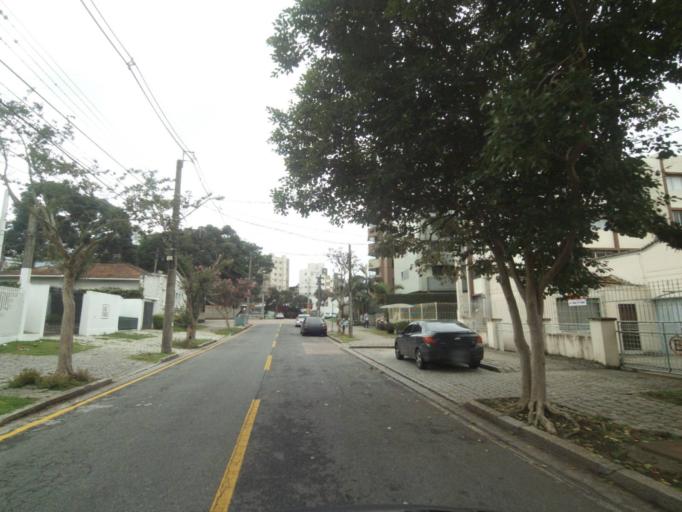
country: BR
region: Parana
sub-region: Curitiba
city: Curitiba
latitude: -25.4207
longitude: -49.2557
